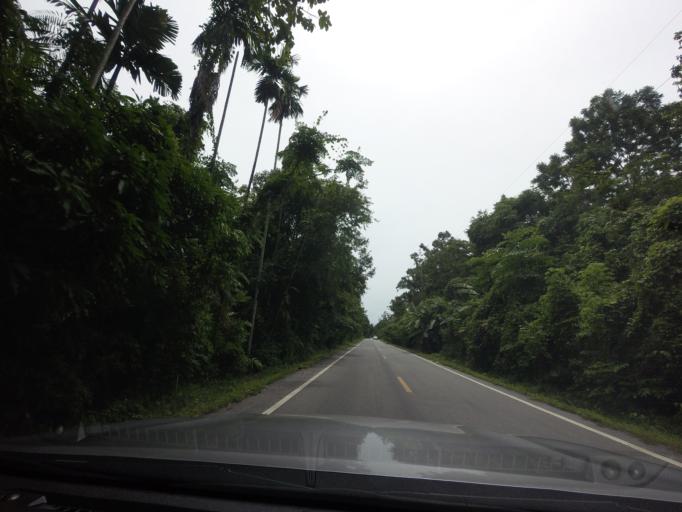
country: TH
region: Pattani
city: Kapho
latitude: 6.6008
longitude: 101.5318
